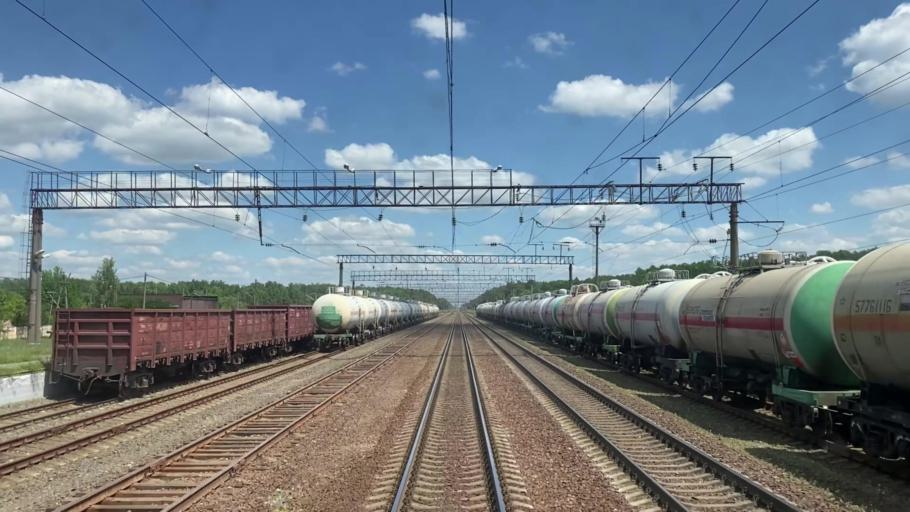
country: BY
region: Brest
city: Pruzhany
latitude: 52.4745
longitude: 24.5358
